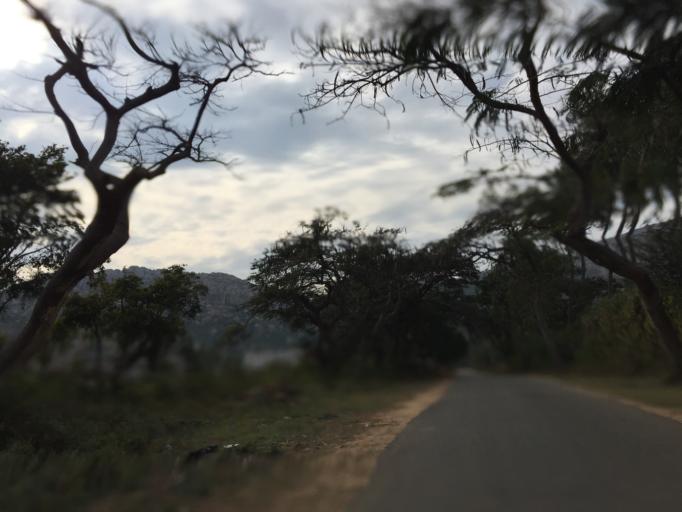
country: IN
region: Karnataka
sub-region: Kolar
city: Kolar
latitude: 13.1383
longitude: 78.1091
